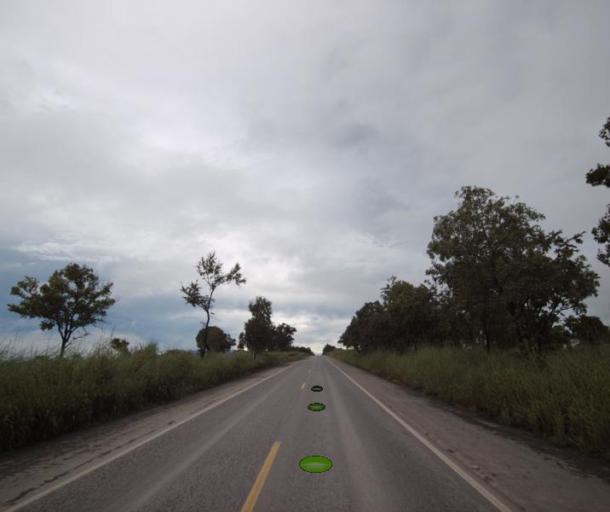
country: BR
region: Goias
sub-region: Porangatu
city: Porangatu
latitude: -13.5375
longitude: -49.1075
